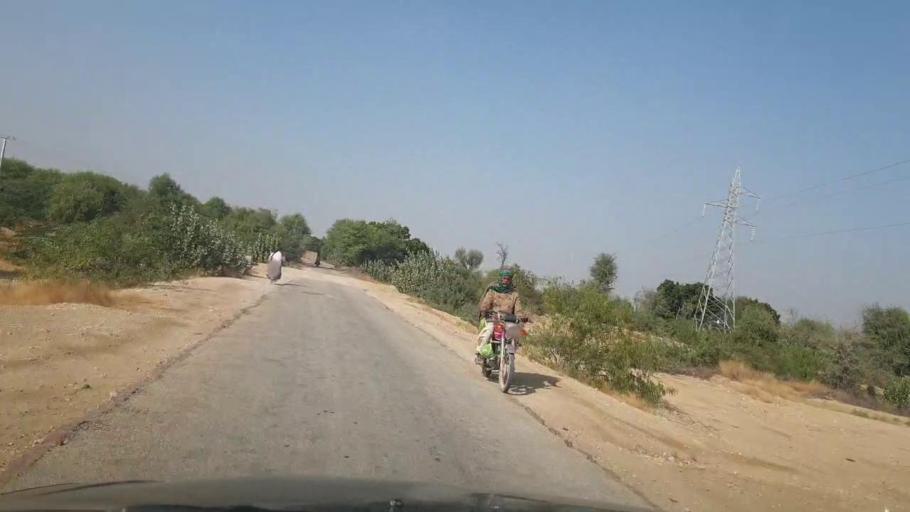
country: PK
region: Sindh
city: Jamshoro
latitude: 25.5248
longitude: 67.8221
